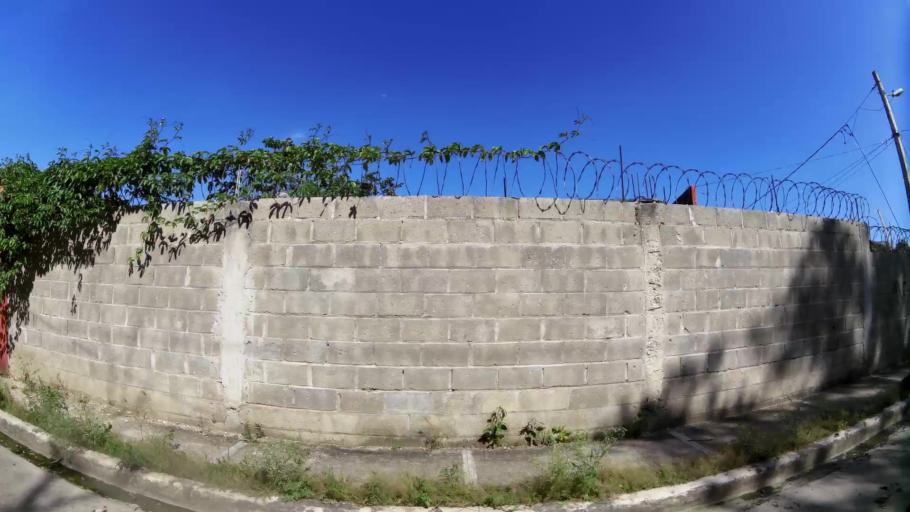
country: DO
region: San Cristobal
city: El Carril
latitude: 18.4731
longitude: -70.0119
